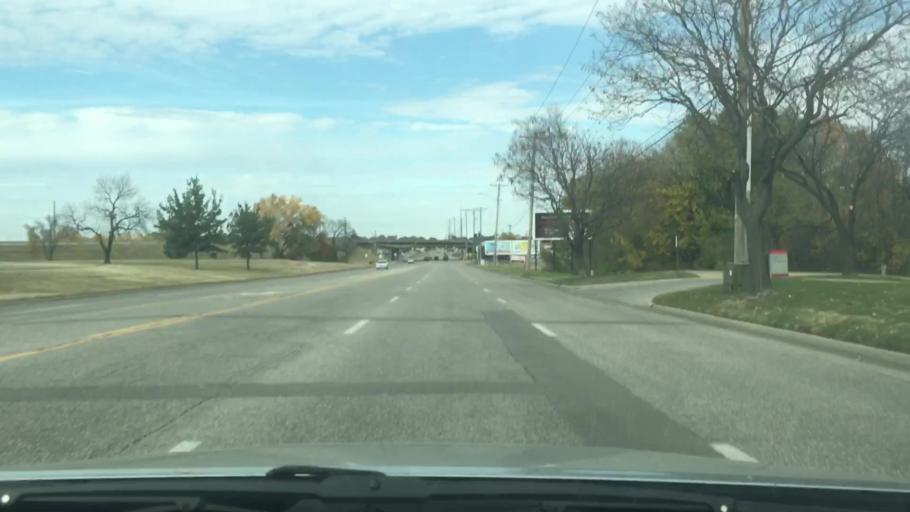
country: US
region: Kansas
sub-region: Sedgwick County
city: Wichita
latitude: 37.6401
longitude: -97.2804
